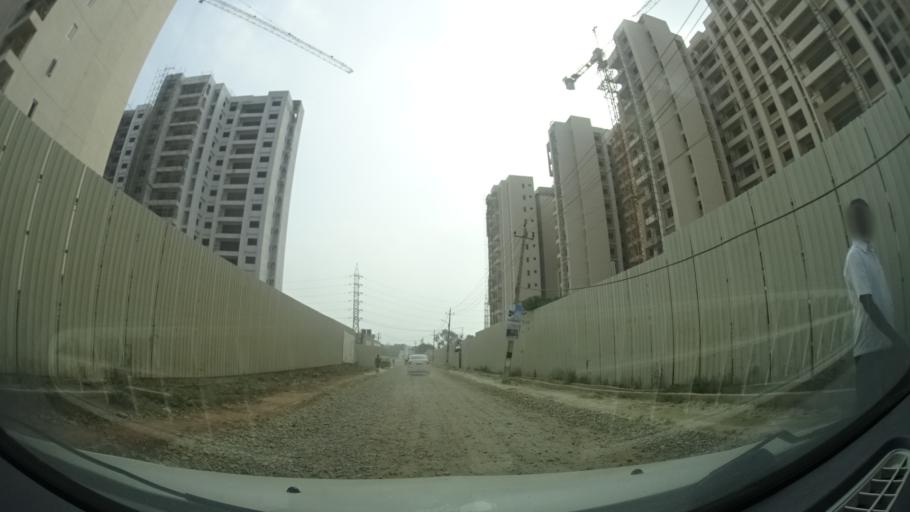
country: IN
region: Karnataka
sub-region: Bangalore Urban
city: Anekal
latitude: 12.8298
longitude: 77.6657
